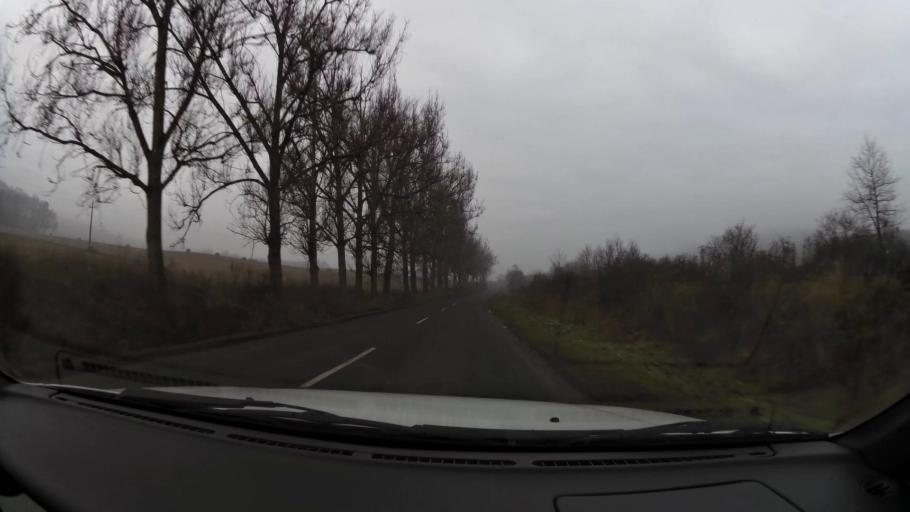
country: HU
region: Borsod-Abauj-Zemplen
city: Rudabanya
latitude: 48.3469
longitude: 20.6421
